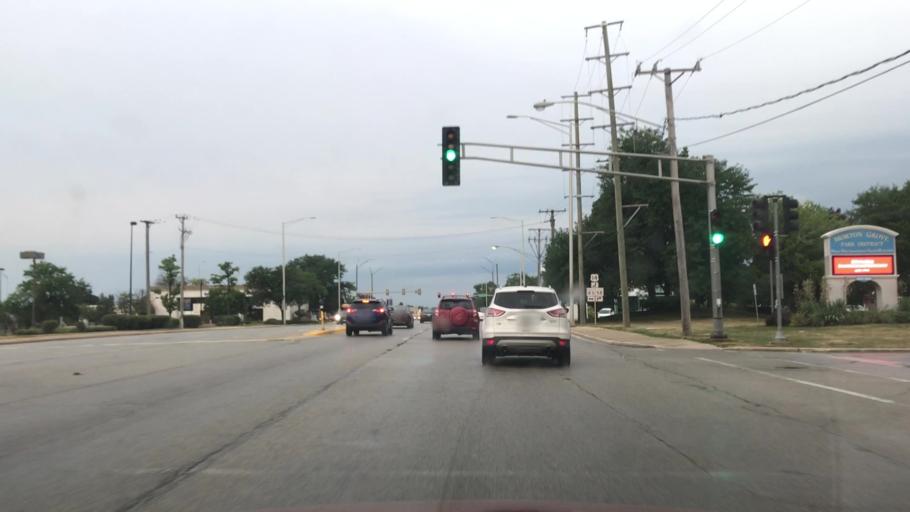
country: US
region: Illinois
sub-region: Cook County
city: Morton Grove
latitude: 42.0409
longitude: -87.7966
